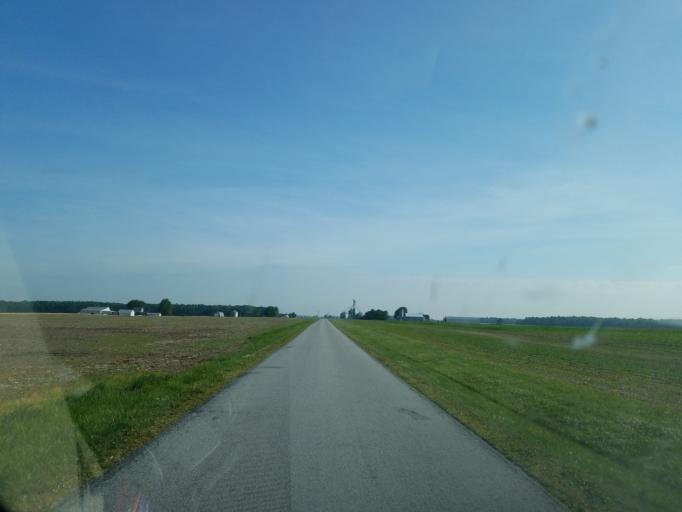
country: US
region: Ohio
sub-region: Hardin County
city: Kenton
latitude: 40.7413
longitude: -83.6716
